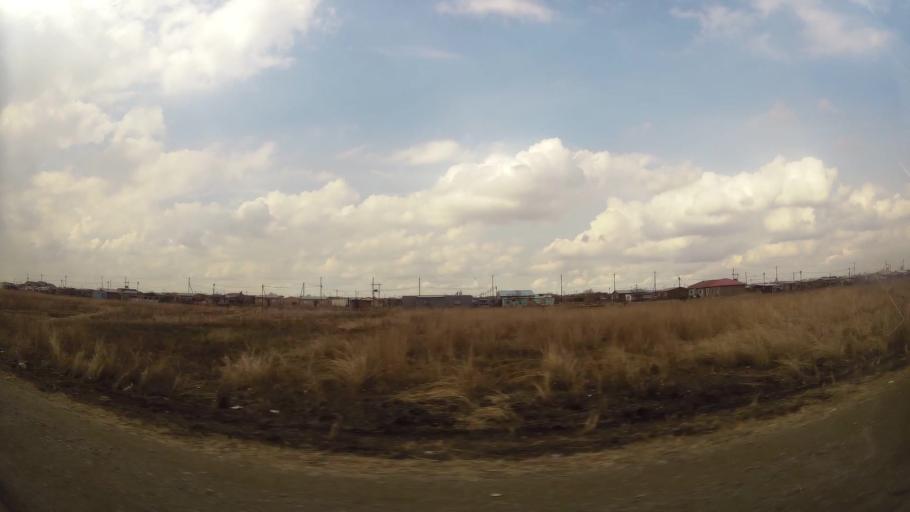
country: ZA
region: Orange Free State
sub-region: Fezile Dabi District Municipality
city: Sasolburg
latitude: -26.8535
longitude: 27.8888
